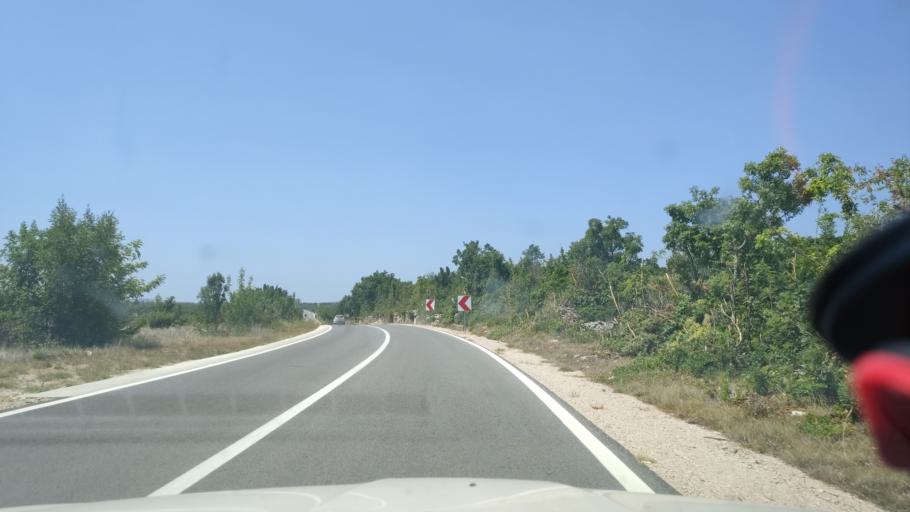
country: HR
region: Sibensko-Kniniska
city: Kistanje
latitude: 43.9703
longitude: 15.8838
